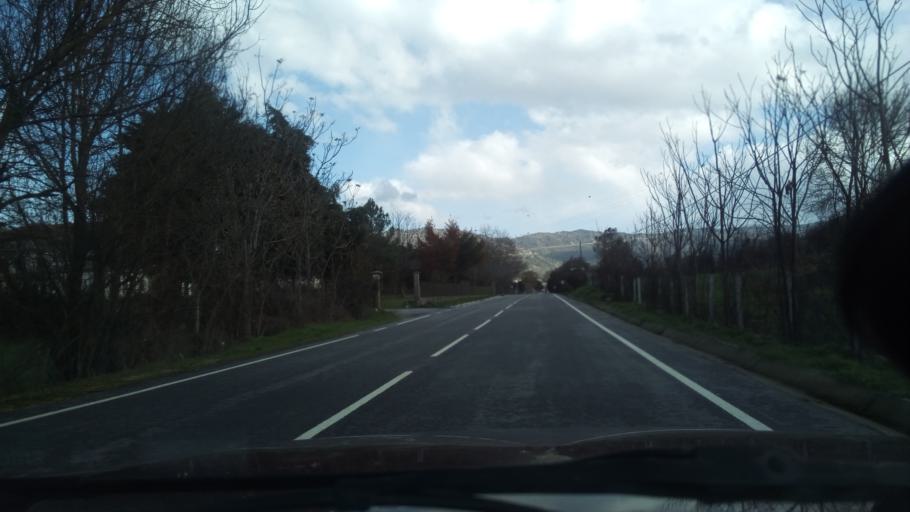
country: PT
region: Guarda
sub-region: Celorico da Beira
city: Celorico da Beira
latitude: 40.6218
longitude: -7.3171
